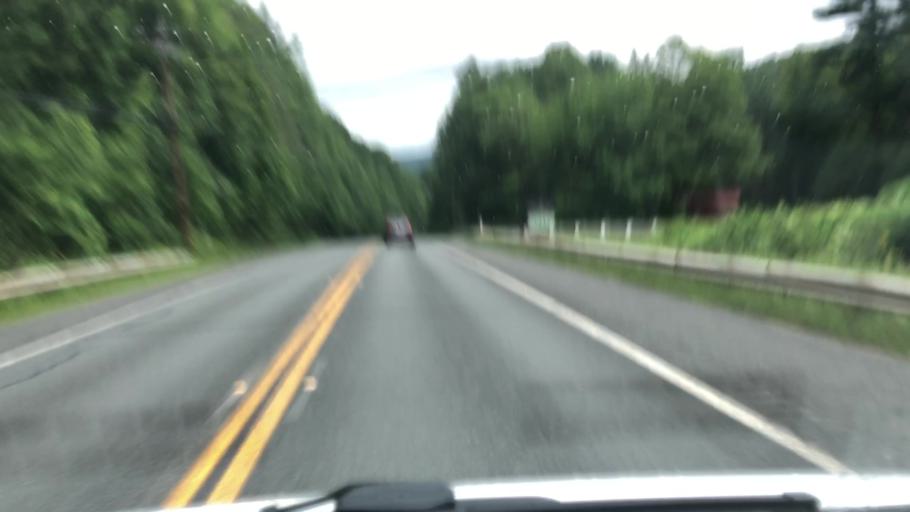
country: US
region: Massachusetts
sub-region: Berkshire County
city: Lanesborough
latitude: 42.6078
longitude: -73.2357
